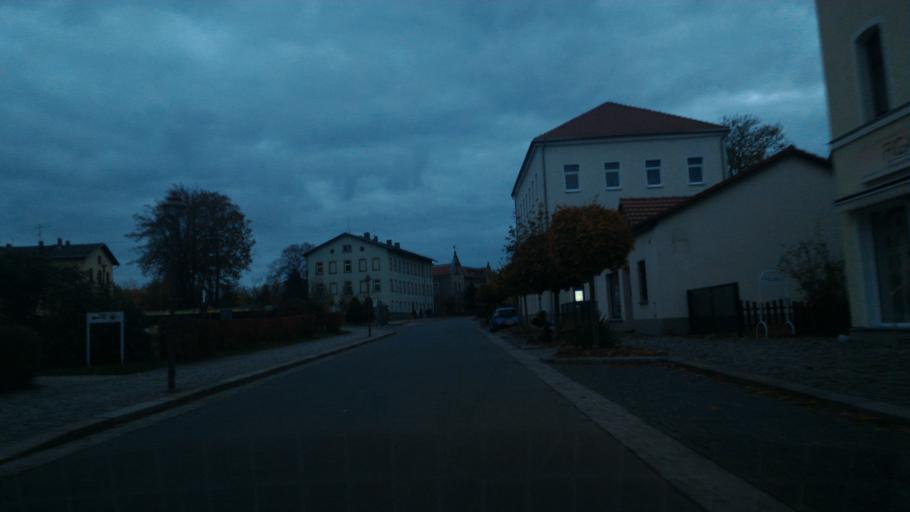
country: DE
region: Saxony
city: Ebersbach
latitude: 51.0052
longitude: 14.5782
